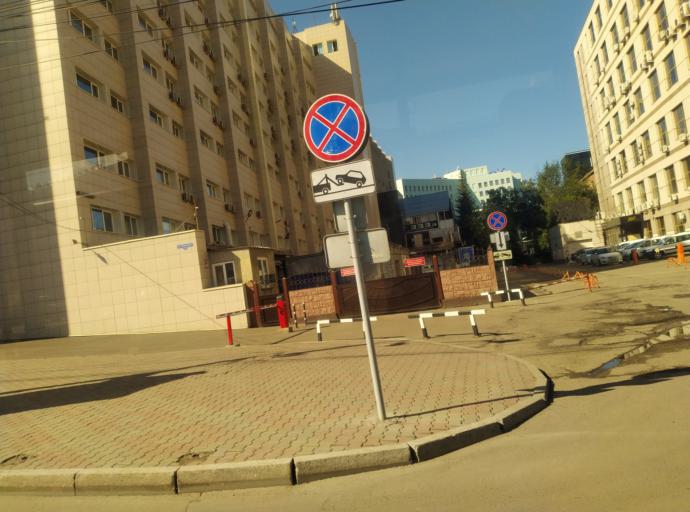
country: RU
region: Krasnoyarskiy
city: Krasnoyarsk
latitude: 56.0097
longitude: 92.8712
